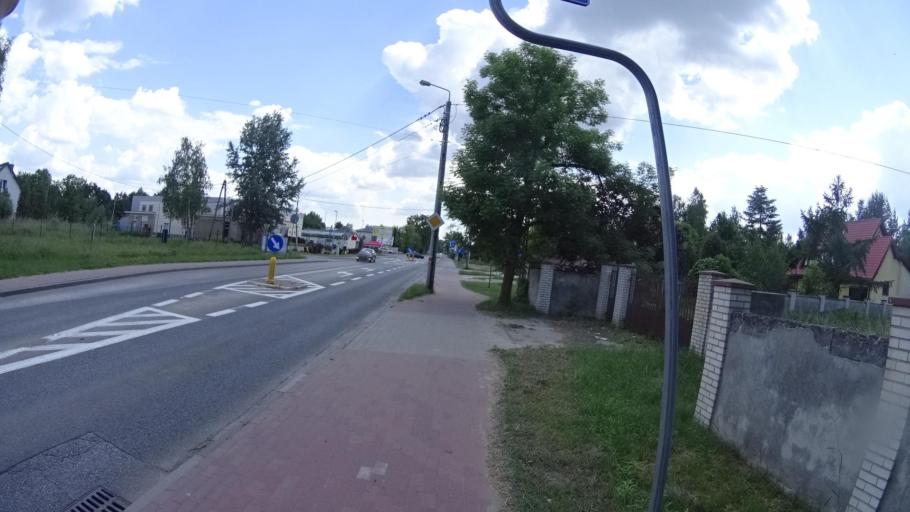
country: PL
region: Masovian Voivodeship
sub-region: Powiat pruszkowski
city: Nadarzyn
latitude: 52.1023
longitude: 20.8040
